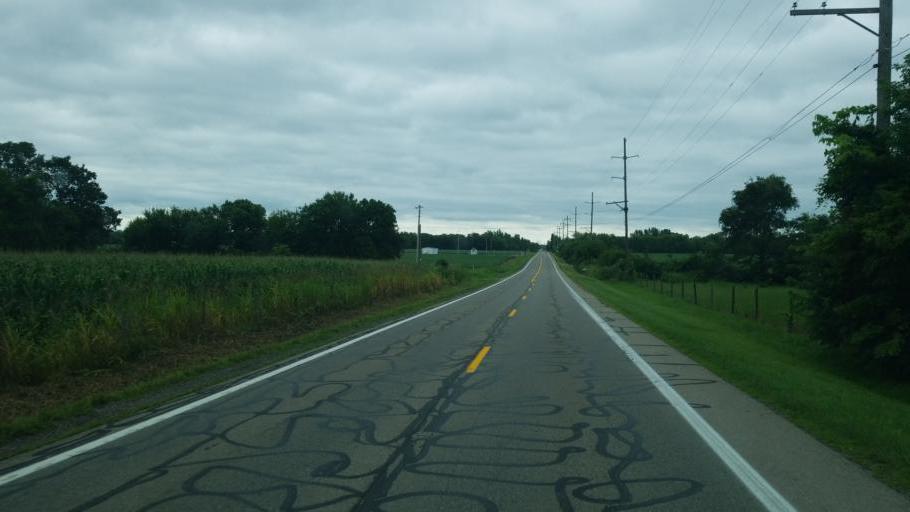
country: US
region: Ohio
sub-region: Pickaway County
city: Commercial Point
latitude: 39.7530
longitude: -83.0246
